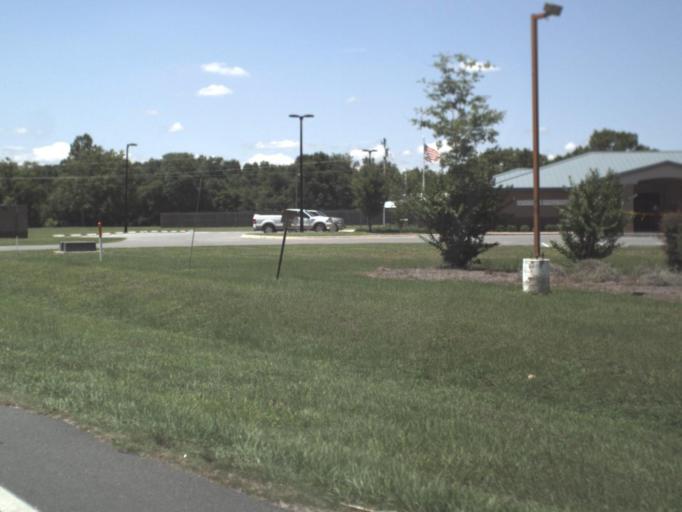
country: US
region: Florida
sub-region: Lafayette County
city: Mayo
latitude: 30.0561
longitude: -83.1834
